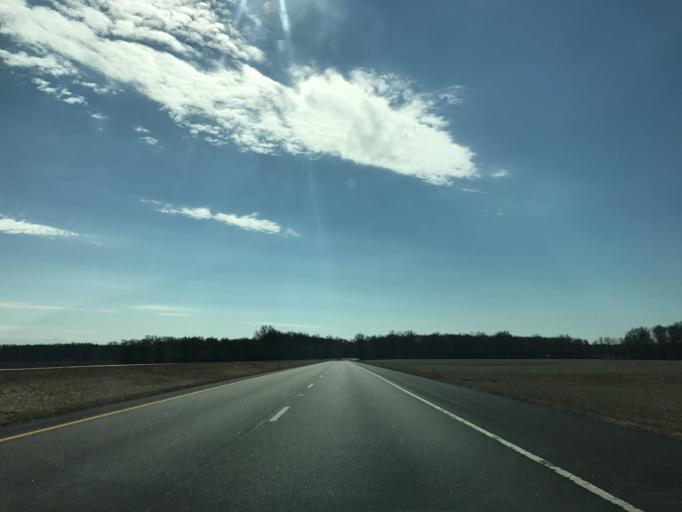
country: US
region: Maryland
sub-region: Queen Anne's County
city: Kingstown
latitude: 39.1505
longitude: -75.9225
